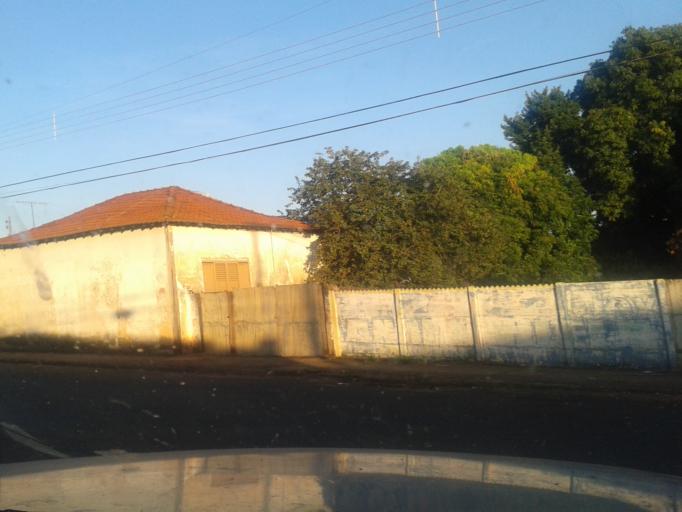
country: BR
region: Minas Gerais
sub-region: Ituiutaba
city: Ituiutaba
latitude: -18.9779
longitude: -49.4679
